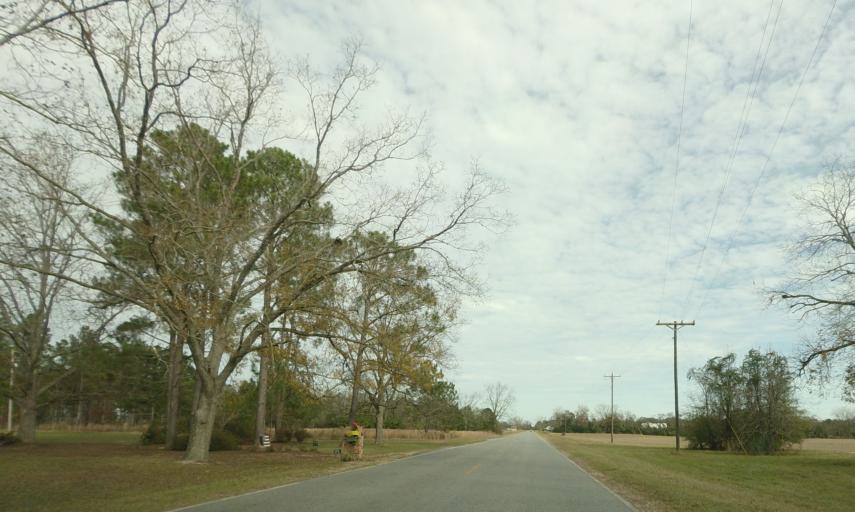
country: US
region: Georgia
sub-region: Dodge County
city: Chester
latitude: 32.4447
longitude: -83.1553
